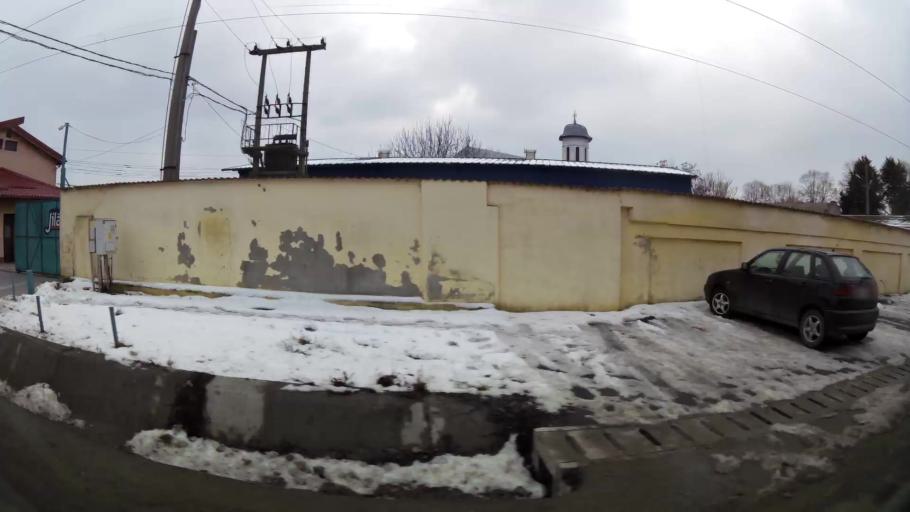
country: RO
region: Ilfov
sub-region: Comuna Afumati
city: Afumati
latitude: 44.5271
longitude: 26.2429
